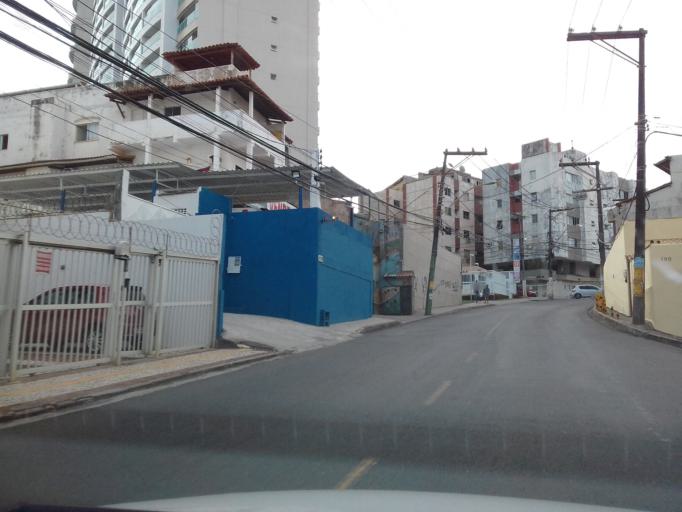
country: BR
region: Bahia
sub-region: Salvador
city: Salvador
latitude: -13.0077
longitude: -38.4959
